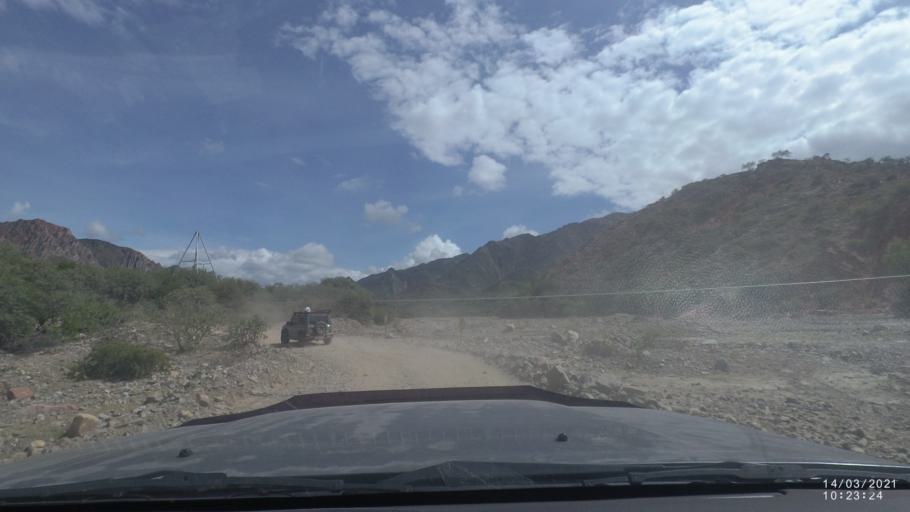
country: BO
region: Cochabamba
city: Cliza
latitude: -17.9173
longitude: -65.8726
